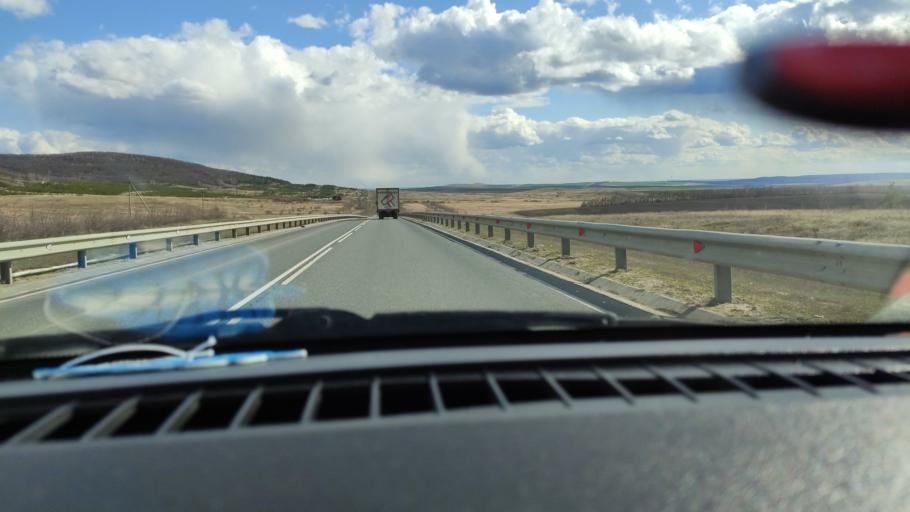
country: RU
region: Saratov
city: Alekseyevka
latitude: 52.3142
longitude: 47.9235
